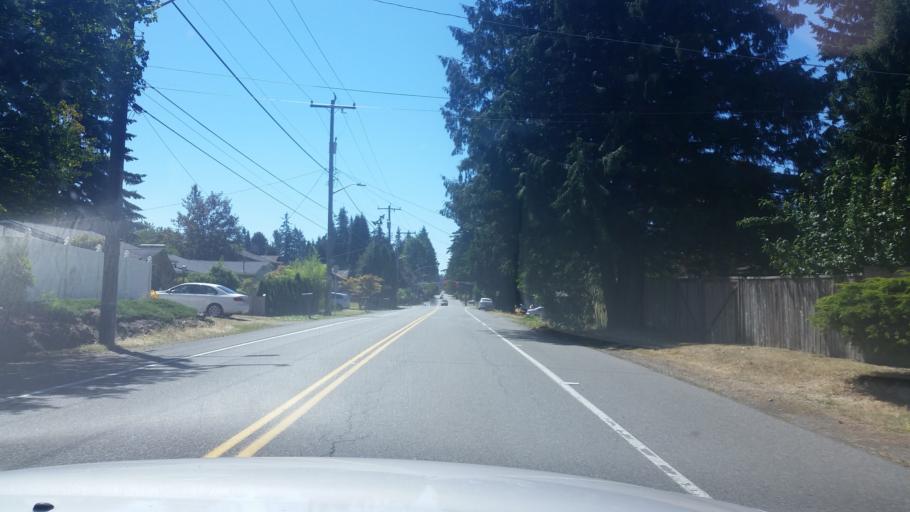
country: US
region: Washington
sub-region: King County
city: Shoreline
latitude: 47.7650
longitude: -122.3513
